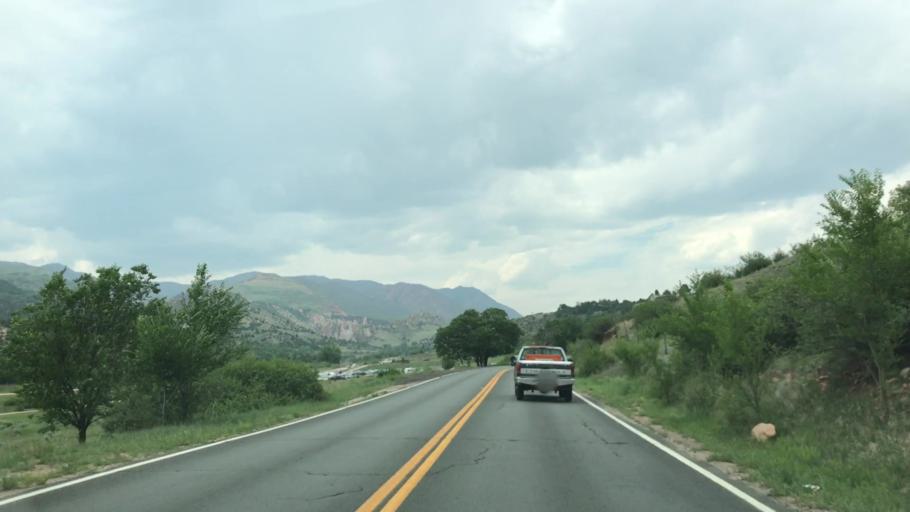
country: US
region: Colorado
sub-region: El Paso County
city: Manitou Springs
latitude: 38.8729
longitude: -104.8686
